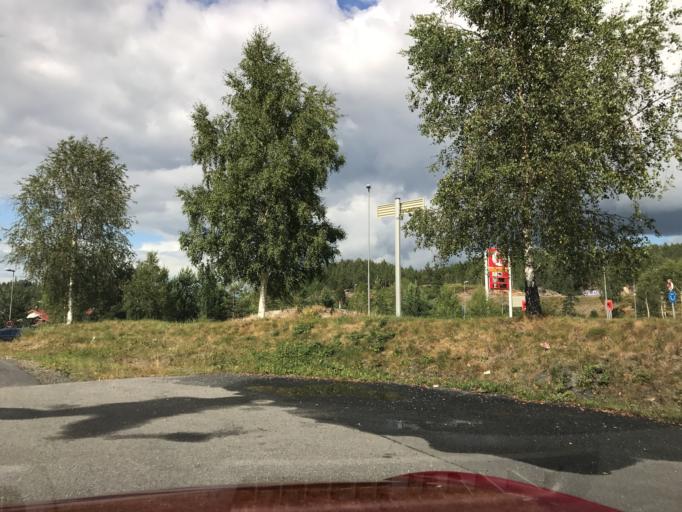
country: NO
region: Aust-Agder
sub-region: Gjerstad
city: Gjerstad
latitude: 58.8208
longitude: 9.0739
